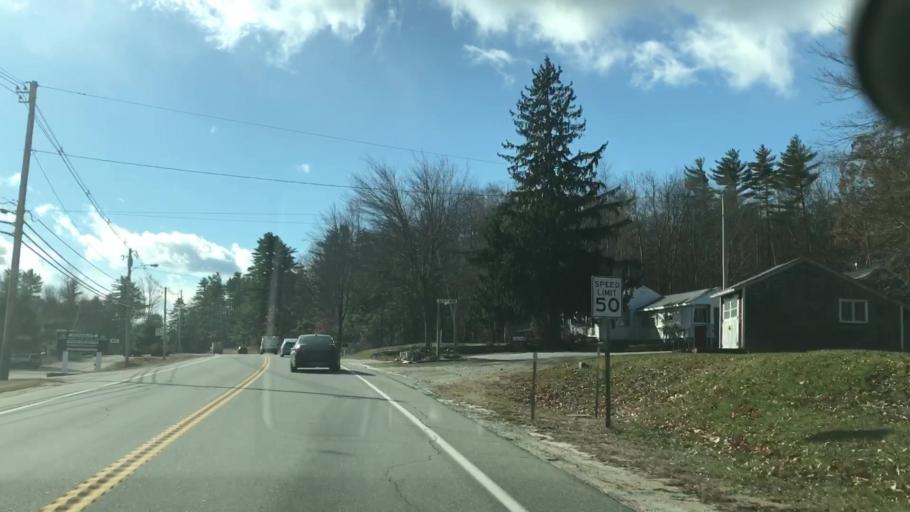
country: US
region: New Hampshire
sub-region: Carroll County
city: Wolfeboro
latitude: 43.6167
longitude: -71.1743
